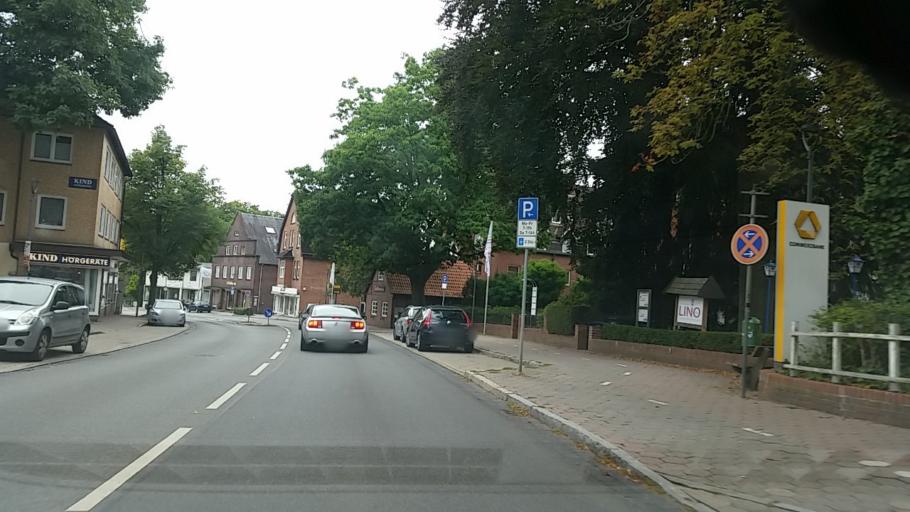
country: DE
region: Schleswig-Holstein
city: Reinbek
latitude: 53.5089
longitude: 10.2510
